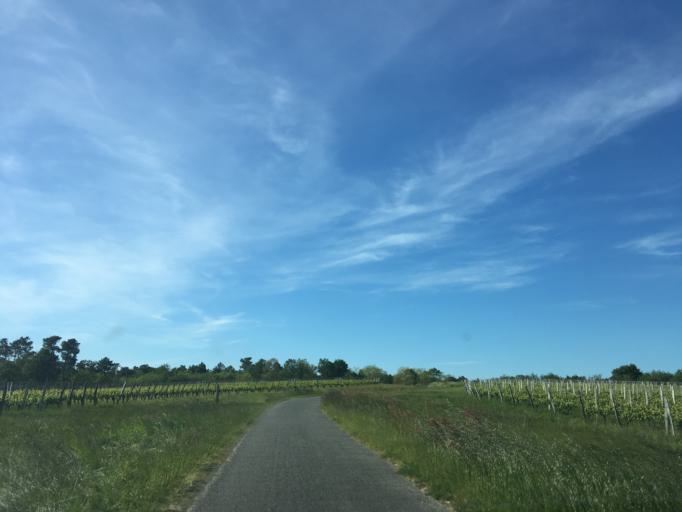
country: FR
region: Poitou-Charentes
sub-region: Departement de la Charente-Maritime
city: Mirambeau
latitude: 45.3370
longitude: -0.5813
